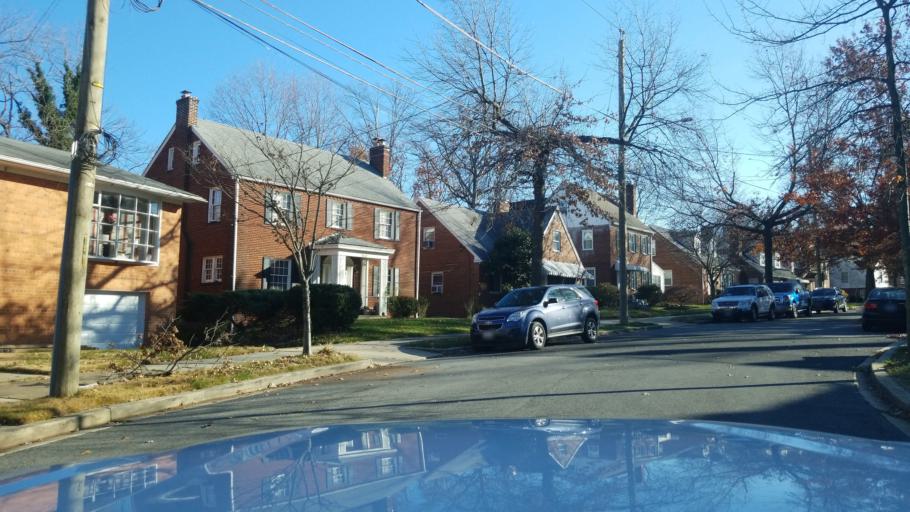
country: US
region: Maryland
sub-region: Prince George's County
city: Silver Hill
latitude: 38.8721
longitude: -76.9533
